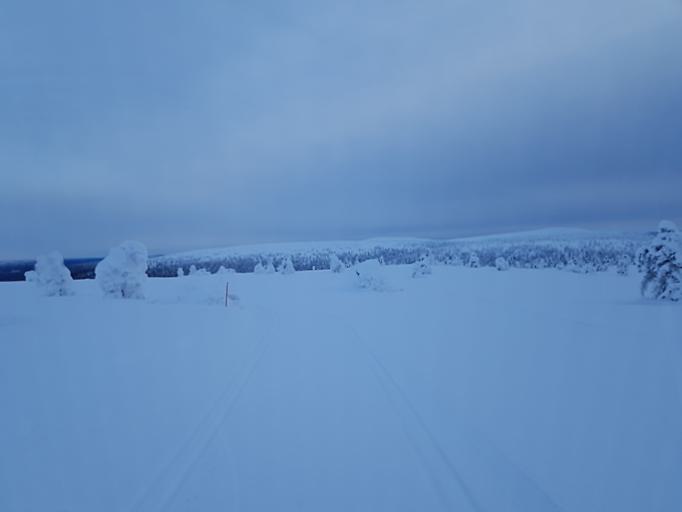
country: FI
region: Lapland
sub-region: Tunturi-Lappi
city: Kolari
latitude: 67.6578
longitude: 24.2246
